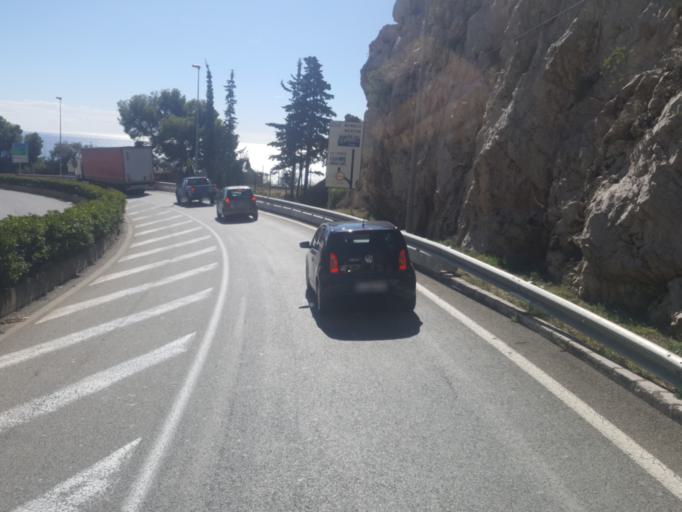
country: FR
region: Provence-Alpes-Cote d'Azur
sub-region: Departement des Alpes-Maritimes
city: Cap-d'Ail
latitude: 43.7257
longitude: 7.3892
